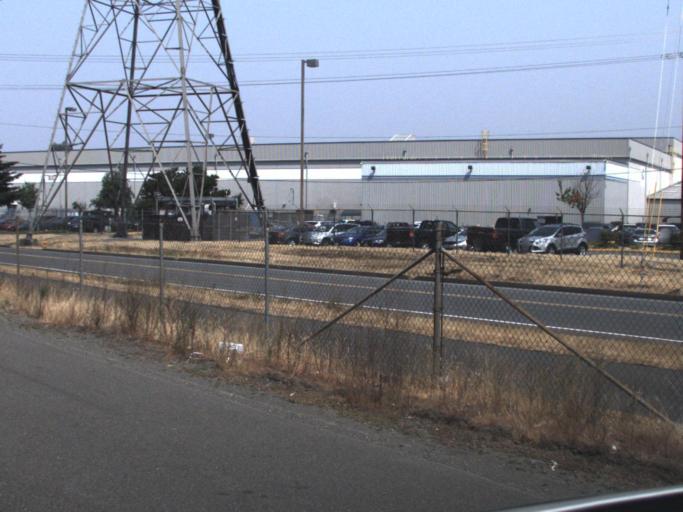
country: US
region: Washington
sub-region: King County
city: Riverton
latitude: 47.5059
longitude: -122.2998
